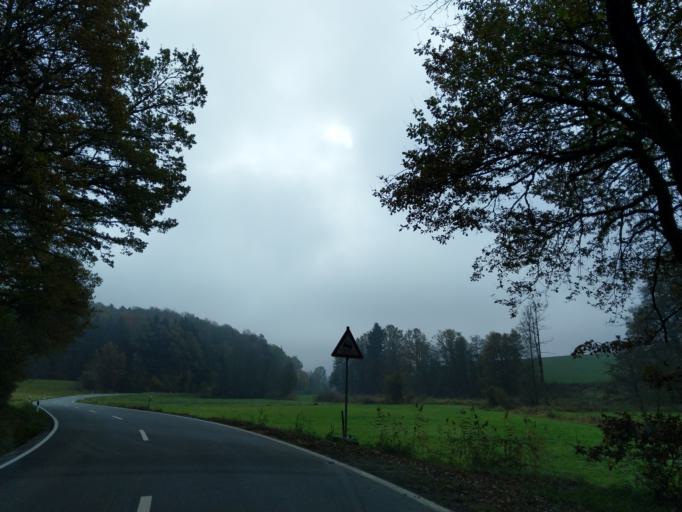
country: DE
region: Bavaria
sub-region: Lower Bavaria
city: Schollnach
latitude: 48.7654
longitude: 13.1780
